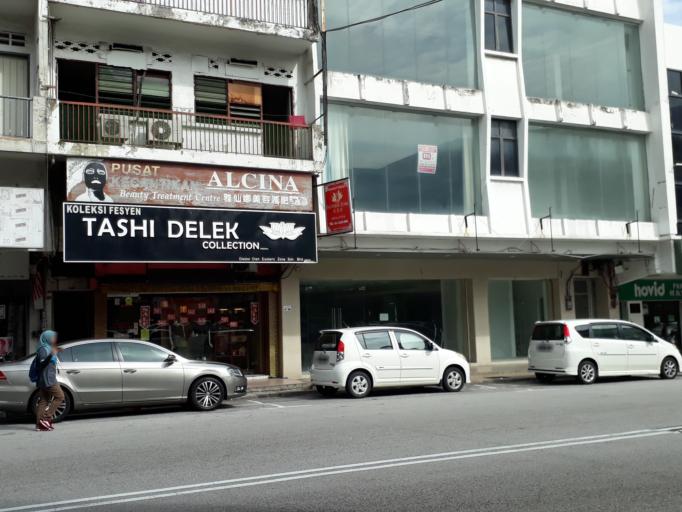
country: MY
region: Perak
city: Ipoh
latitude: 4.5911
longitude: 101.0844
